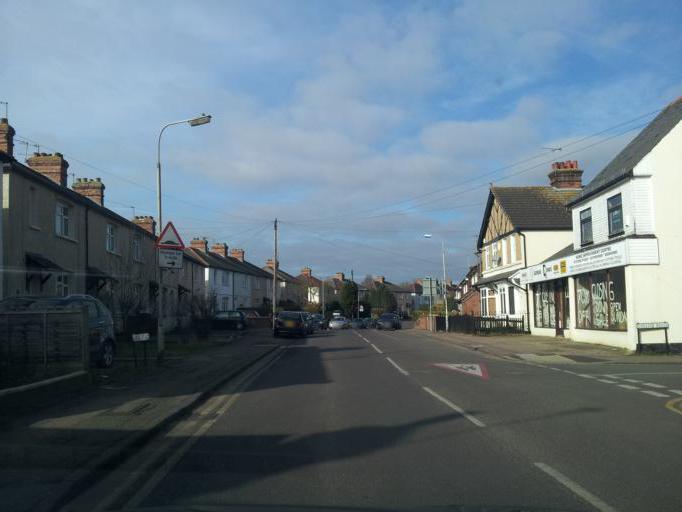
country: GB
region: England
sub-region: Hertfordshire
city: St Albans
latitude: 51.7470
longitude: -0.3097
